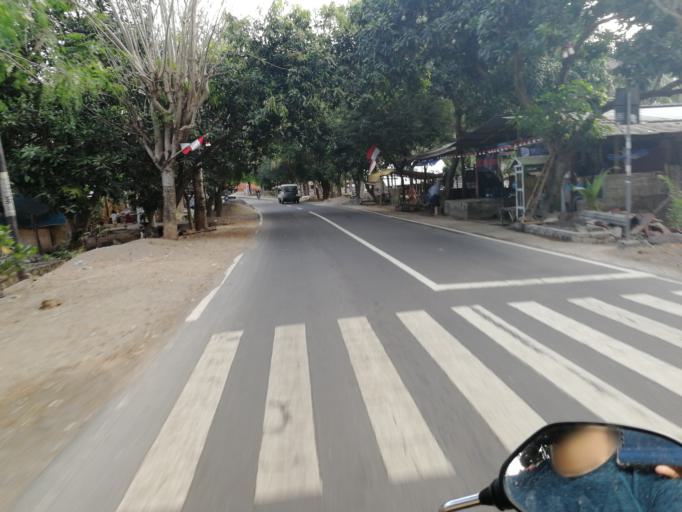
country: ID
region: West Nusa Tenggara
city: Karangsubagan
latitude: -8.4525
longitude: 116.0405
